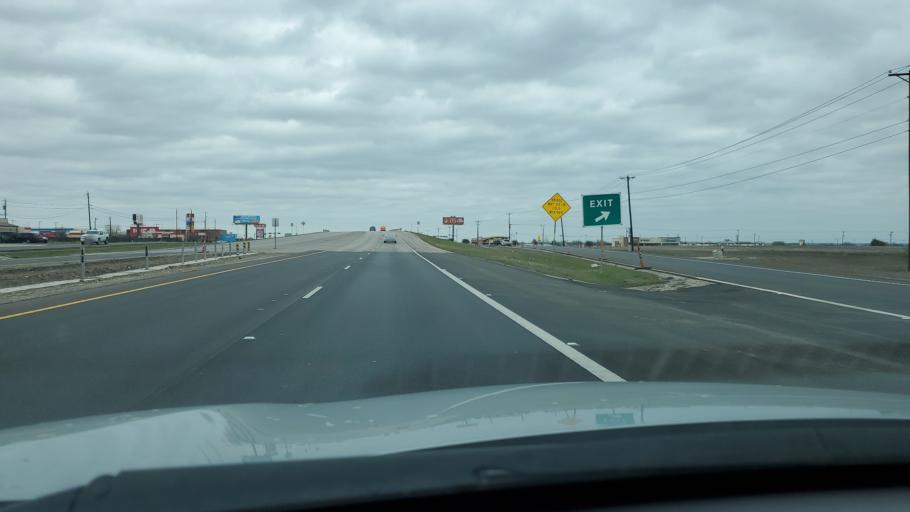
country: US
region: Texas
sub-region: Bell County
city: Killeen
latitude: 31.0750
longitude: -97.7593
